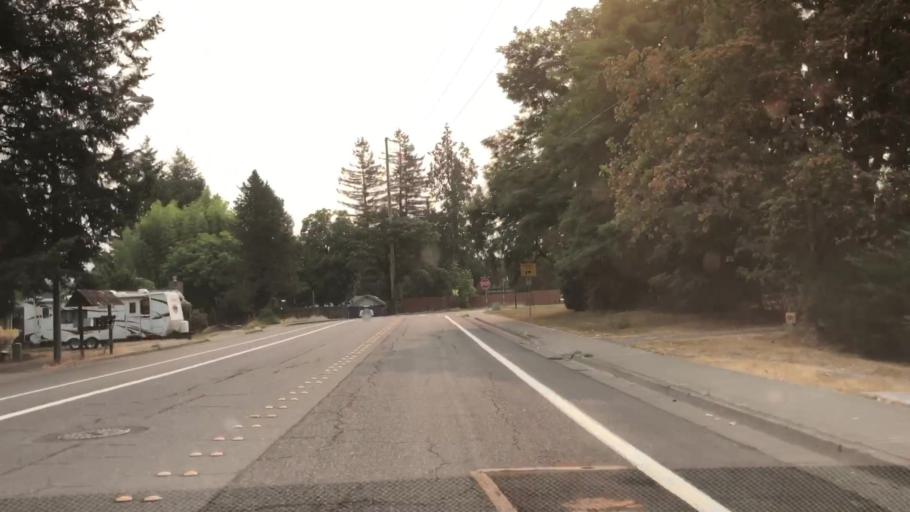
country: US
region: Washington
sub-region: King County
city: Redmond
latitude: 47.6606
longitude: -122.1337
